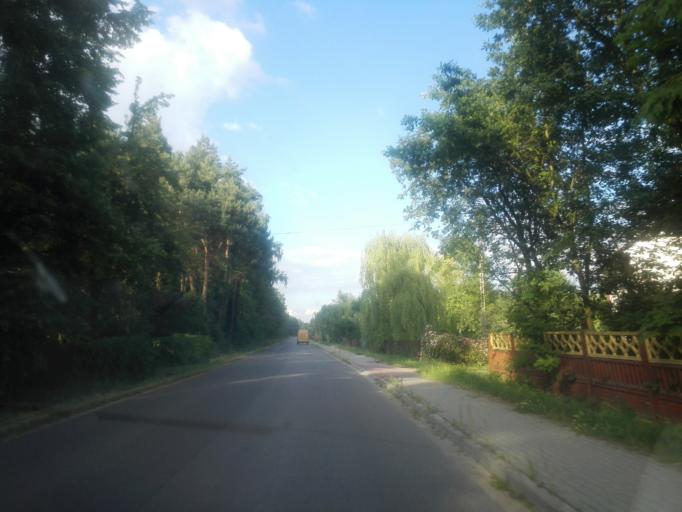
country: PL
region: Swietokrzyskie
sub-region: Powiat jedrzejowski
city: Slupia
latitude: 50.7104
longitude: 19.9701
